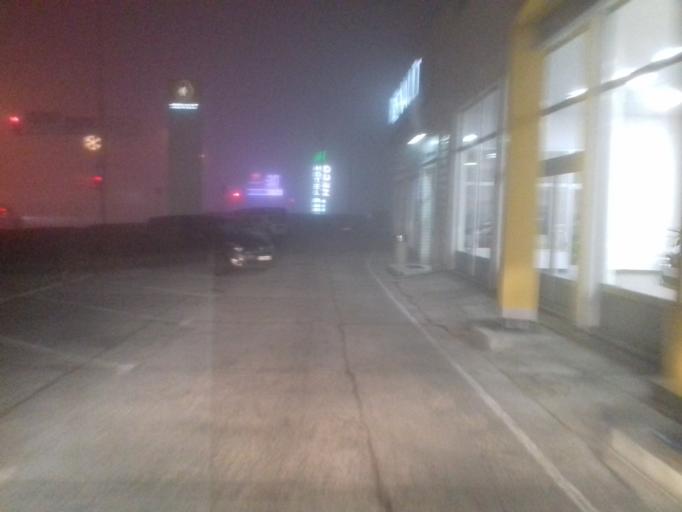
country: BA
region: Federation of Bosnia and Herzegovina
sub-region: Kanton Sarajevo
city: Sarajevo
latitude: 43.8447
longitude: 18.3349
